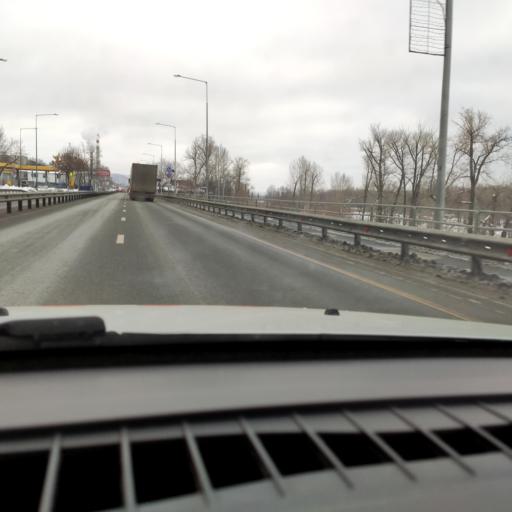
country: RU
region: Samara
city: Volzhskiy
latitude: 53.3871
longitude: 50.1618
